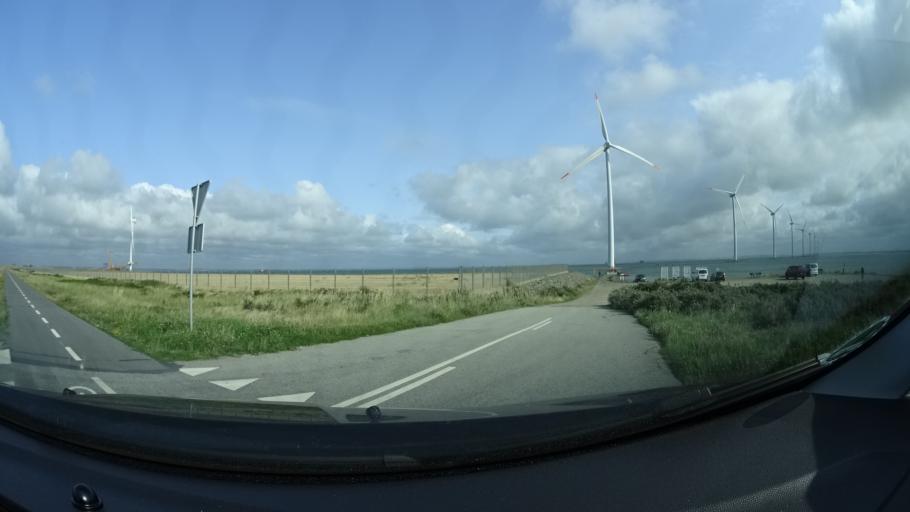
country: DK
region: Central Jutland
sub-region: Lemvig Kommune
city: Thyboron
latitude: 56.6719
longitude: 8.2126
